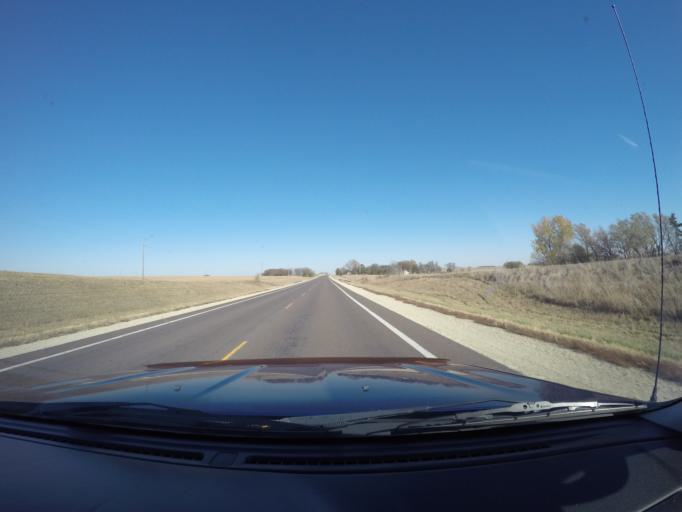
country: US
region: Kansas
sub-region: Marshall County
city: Blue Rapids
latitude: 39.6220
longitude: -96.7502
